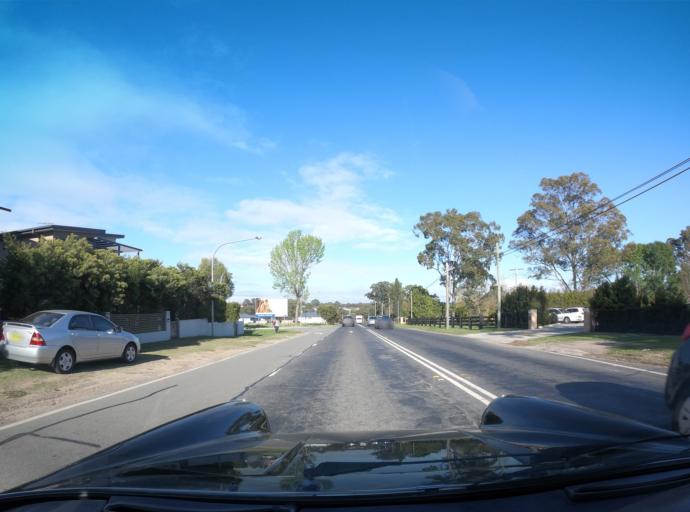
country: AU
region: New South Wales
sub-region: The Hills Shire
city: Beaumont Hills
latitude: -33.6867
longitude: 150.9477
